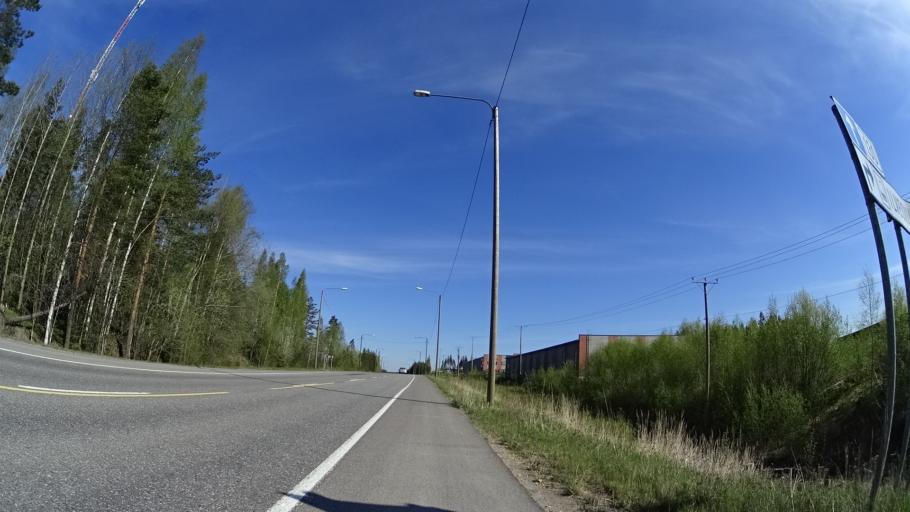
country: FI
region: Uusimaa
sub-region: Helsinki
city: Nurmijaervi
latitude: 60.4509
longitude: 24.8336
